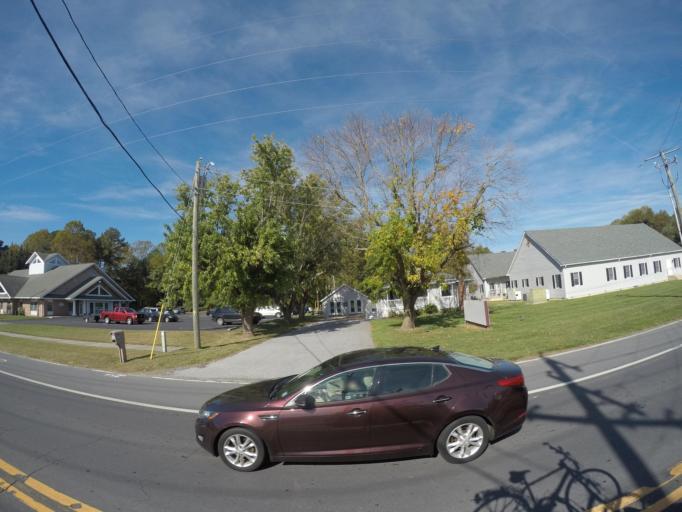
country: US
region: Delaware
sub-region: Sussex County
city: Lewes
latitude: 38.7600
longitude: -75.1543
